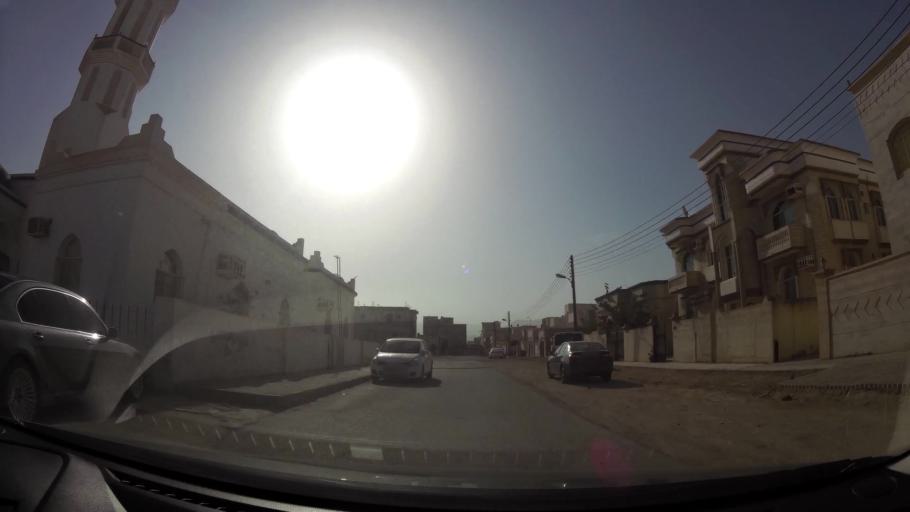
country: OM
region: Zufar
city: Salalah
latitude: 17.0143
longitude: 54.0180
